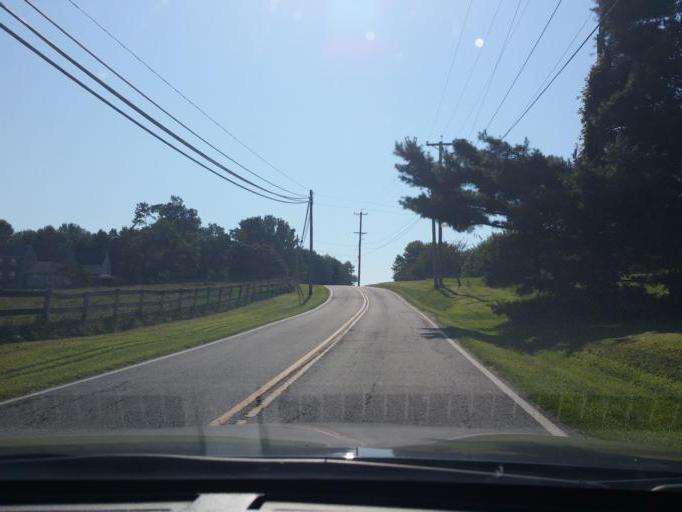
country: US
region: Maryland
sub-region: Cecil County
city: Rising Sun
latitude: 39.6499
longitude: -76.1413
